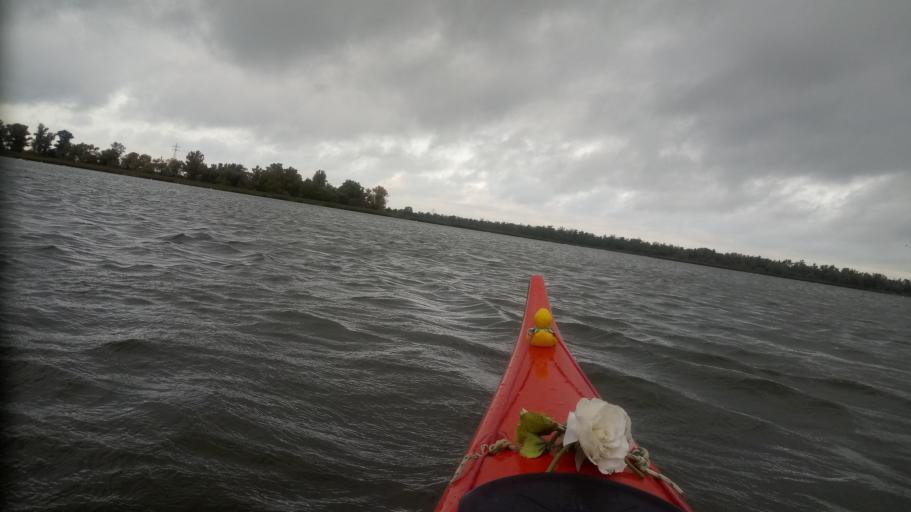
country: NL
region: North Brabant
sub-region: Gemeente Geertruidenberg
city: Geertruidenberg
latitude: 51.7379
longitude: 4.8384
